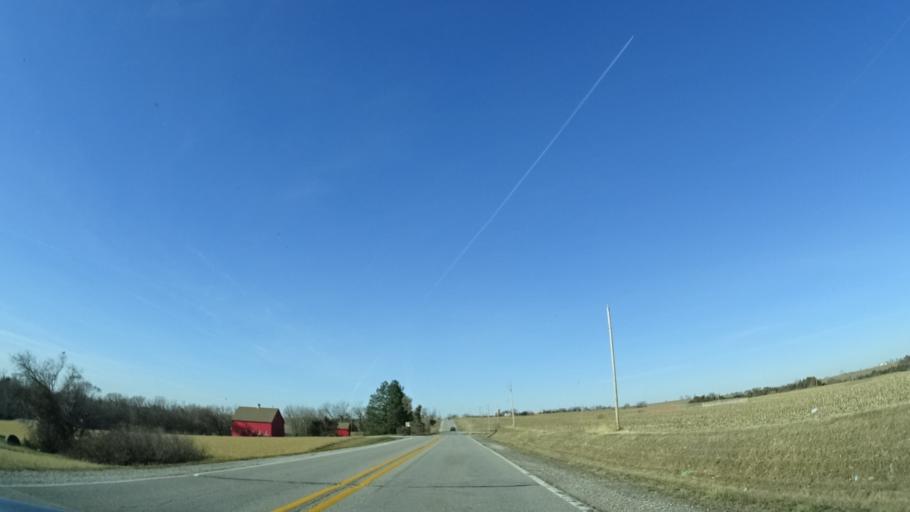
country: US
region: Nebraska
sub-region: Sarpy County
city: Papillion
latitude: 41.0890
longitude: -96.0588
